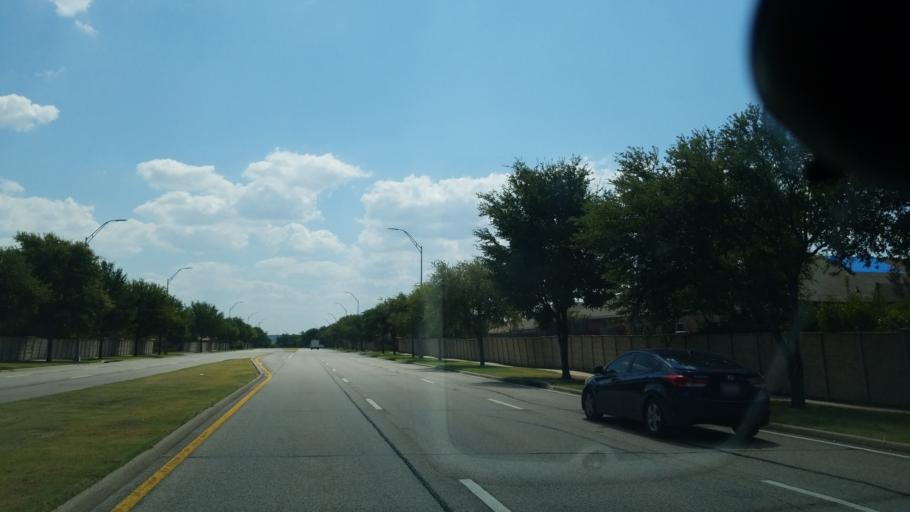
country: US
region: Texas
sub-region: Dallas County
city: Grand Prairie
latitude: 32.7082
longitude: -96.9911
